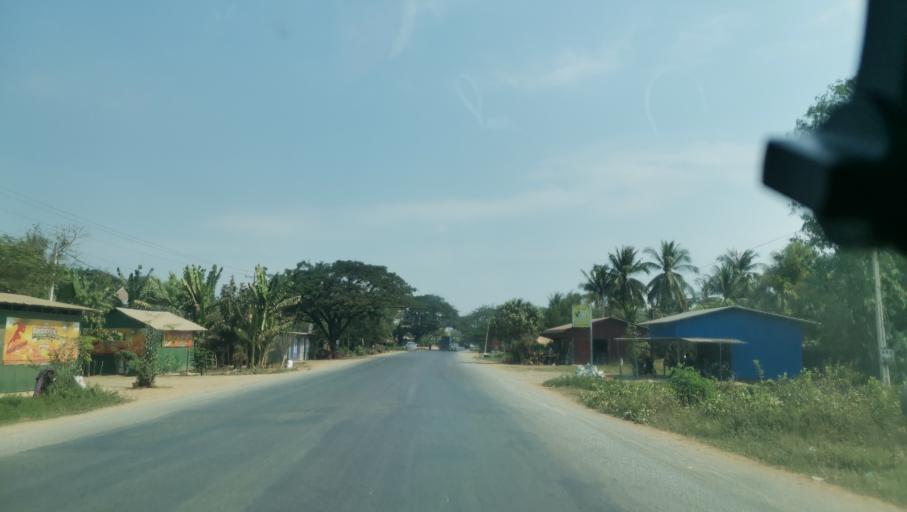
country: KH
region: Battambang
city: Battambang
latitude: 13.0677
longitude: 103.1615
